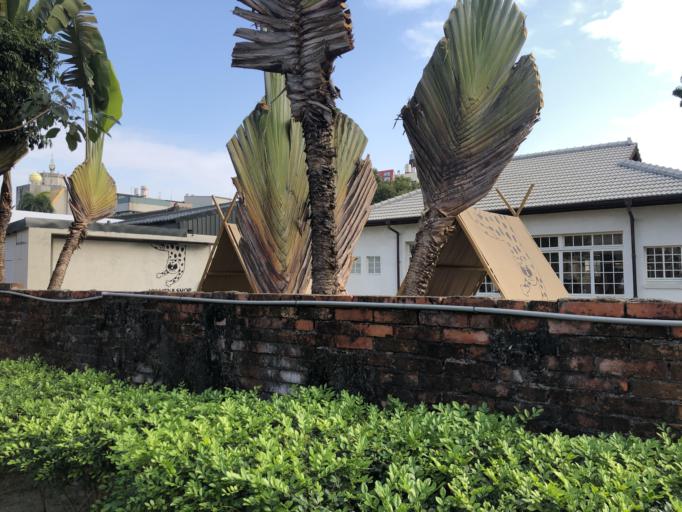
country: TW
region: Taiwan
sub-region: Pingtung
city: Pingtung
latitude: 22.6780
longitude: 120.4842
